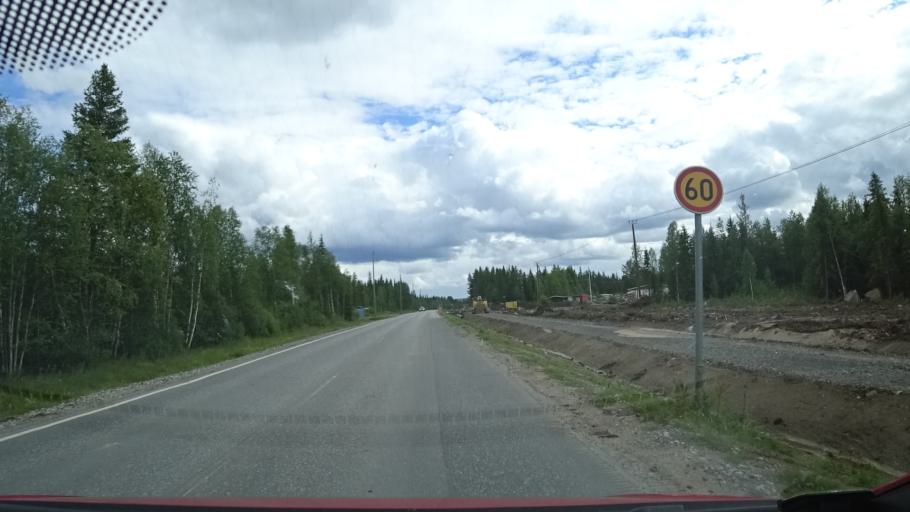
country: FI
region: Lapland
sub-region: Rovaniemi
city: Rovaniemi
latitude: 66.5384
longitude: 25.7225
